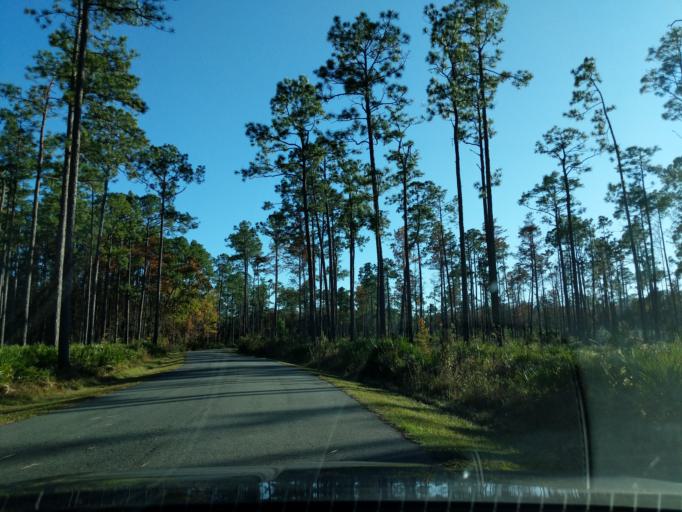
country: US
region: Georgia
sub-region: Charlton County
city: Folkston
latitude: 30.7158
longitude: -82.1409
